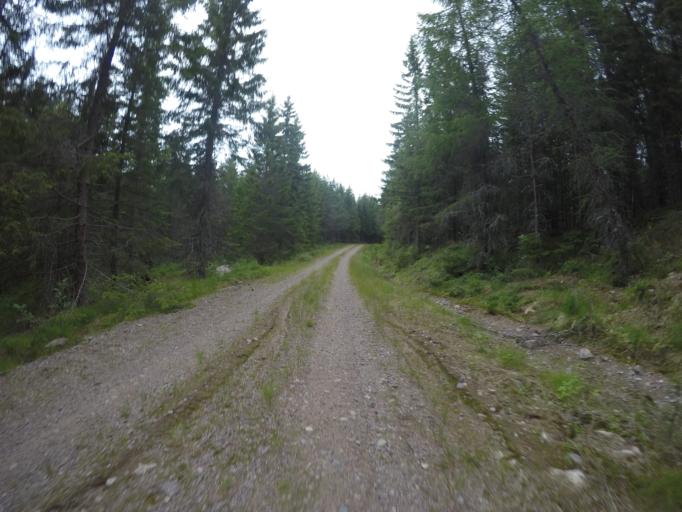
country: SE
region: Vaermland
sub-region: Filipstads Kommun
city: Lesjofors
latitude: 60.1962
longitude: 14.2506
